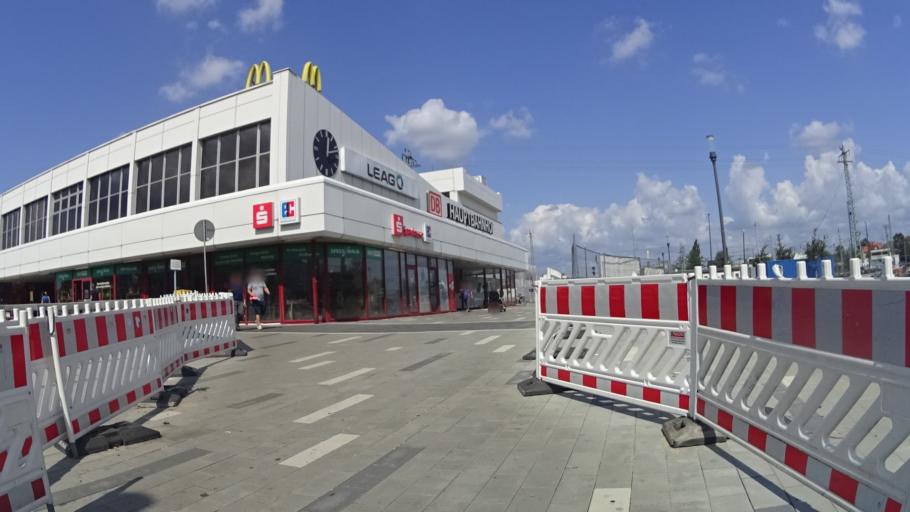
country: DE
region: Brandenburg
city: Cottbus
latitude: 51.7500
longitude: 14.3259
